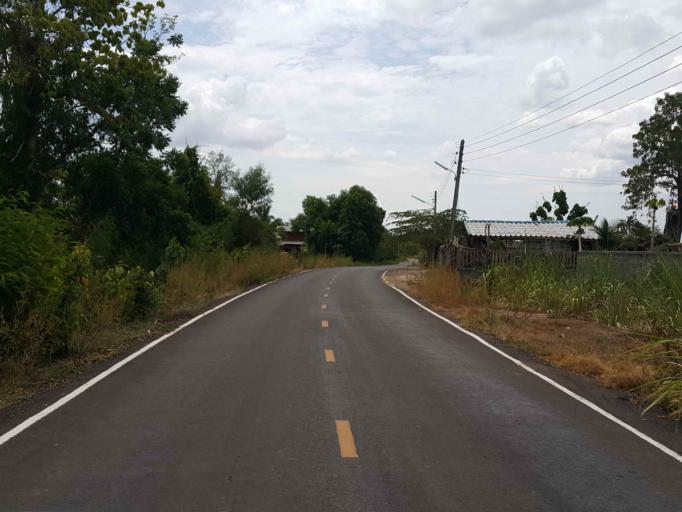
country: TH
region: Sukhothai
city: Thung Saliam
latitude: 17.3280
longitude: 99.5520
